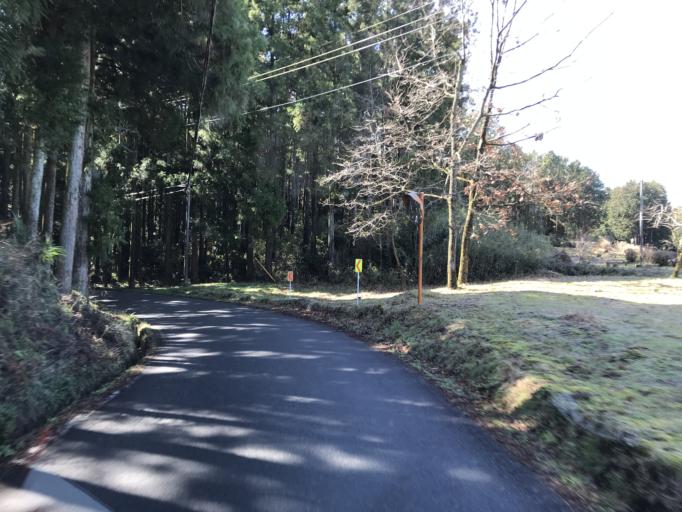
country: JP
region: Shizuoka
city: Fujinomiya
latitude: 35.2505
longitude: 138.6615
